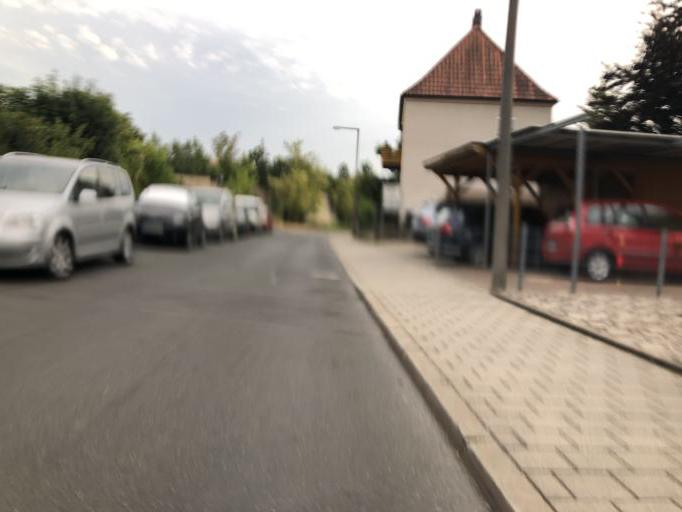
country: DE
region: Bavaria
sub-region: Regierungsbezirk Mittelfranken
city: Erlangen
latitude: 49.5900
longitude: 10.9934
